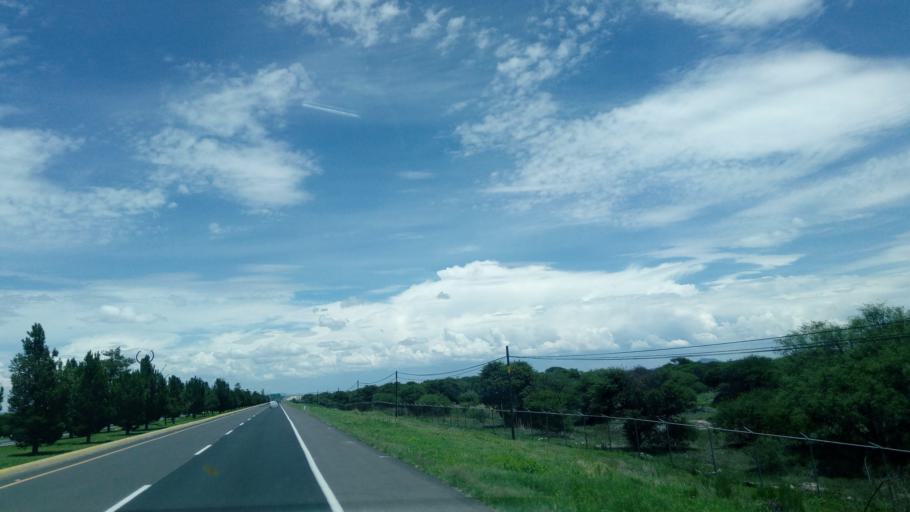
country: MX
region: Durango
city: Victoria de Durango
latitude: 24.1194
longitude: -104.5444
